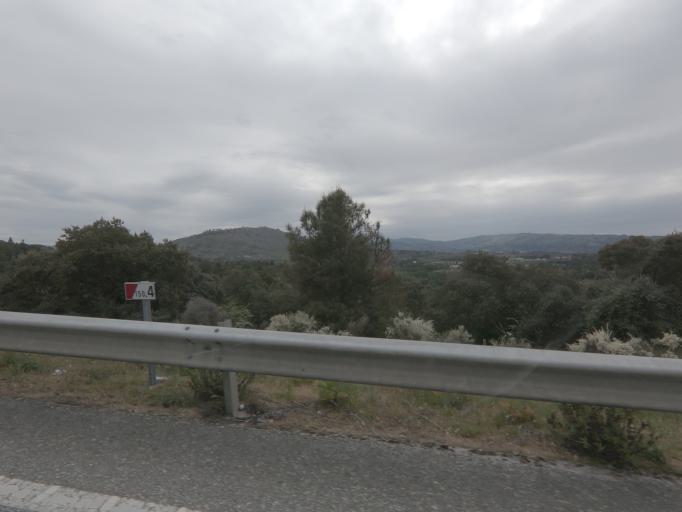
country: PT
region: Guarda
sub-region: Celorico da Beira
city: Celorico da Beira
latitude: 40.6326
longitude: -7.3136
